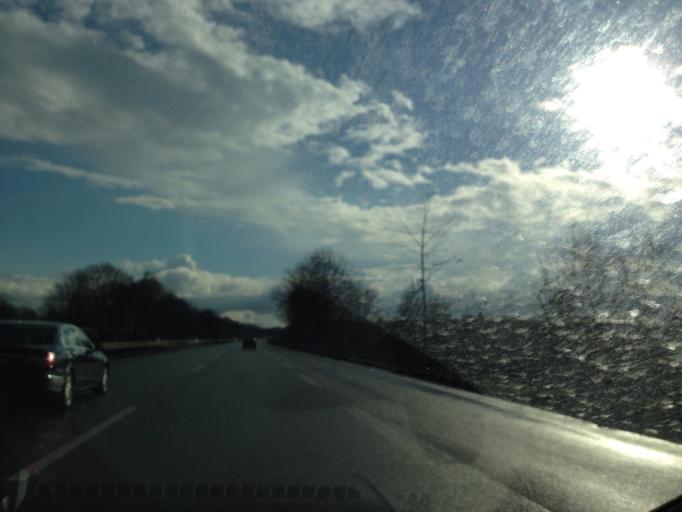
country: DE
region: North Rhine-Westphalia
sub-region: Regierungsbezirk Dusseldorf
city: Neubrueck
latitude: 51.1345
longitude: 6.6099
